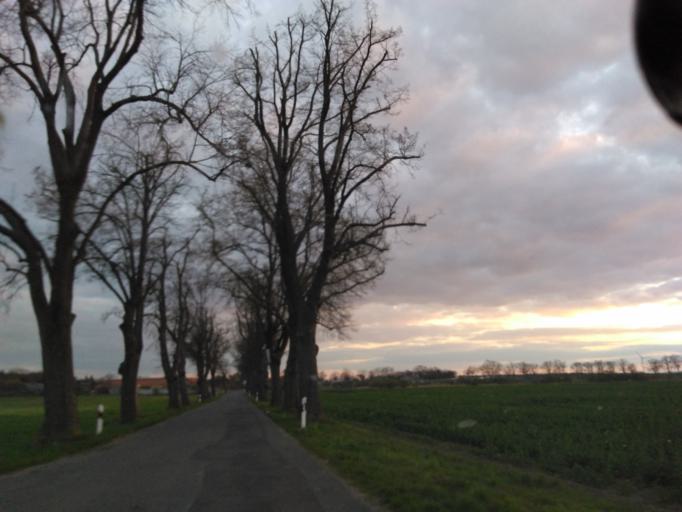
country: DE
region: Brandenburg
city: Protzel
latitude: 52.6556
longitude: 14.0685
